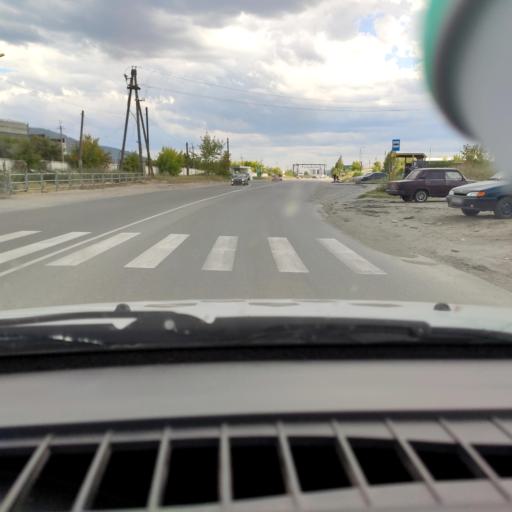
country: RU
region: Chelyabinsk
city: Miass
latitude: 55.0717
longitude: 60.0985
